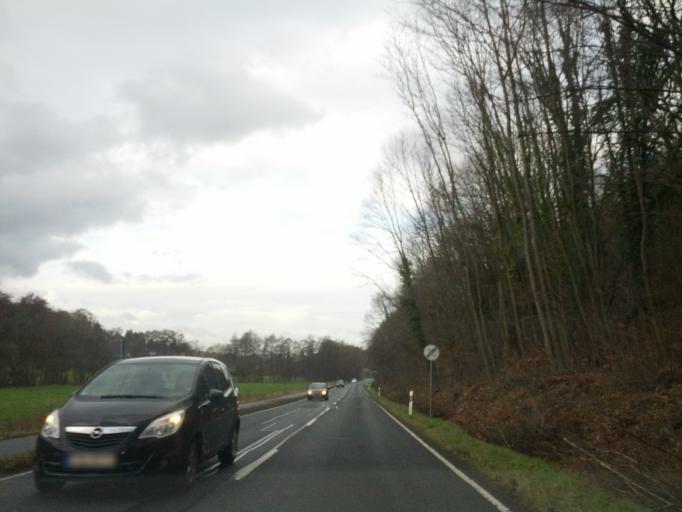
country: DE
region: Hesse
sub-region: Regierungsbezirk Kassel
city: Helsa
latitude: 51.2768
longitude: 9.6535
